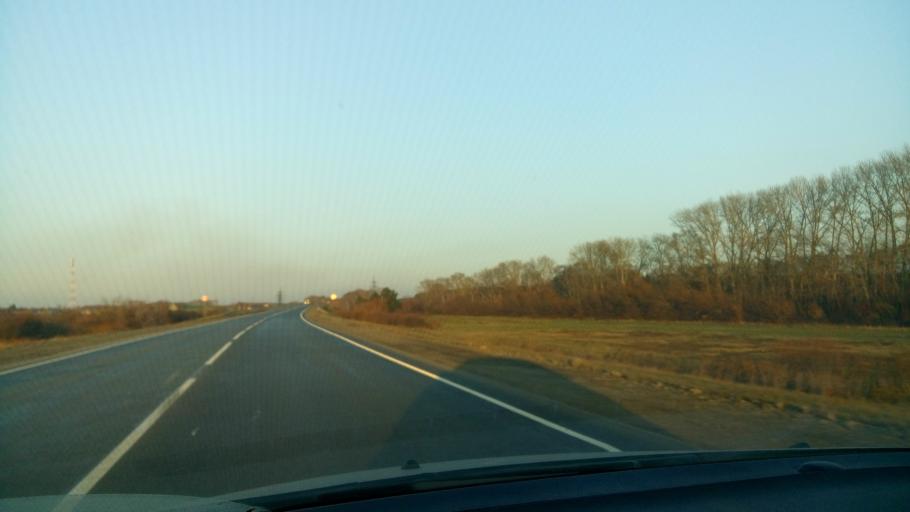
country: RU
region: Sverdlovsk
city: Obukhovskoye
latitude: 56.8371
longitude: 62.5766
